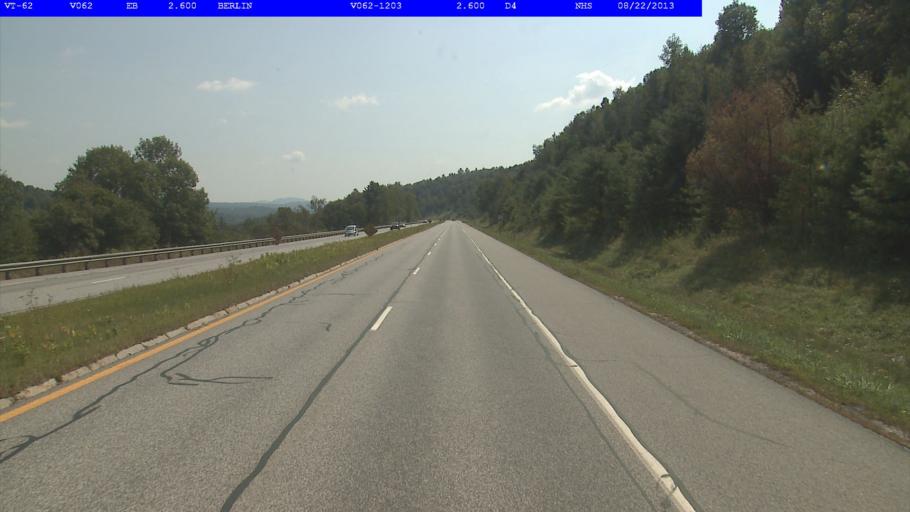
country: US
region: Vermont
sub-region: Washington County
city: Barre
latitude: 44.2152
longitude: -72.5396
